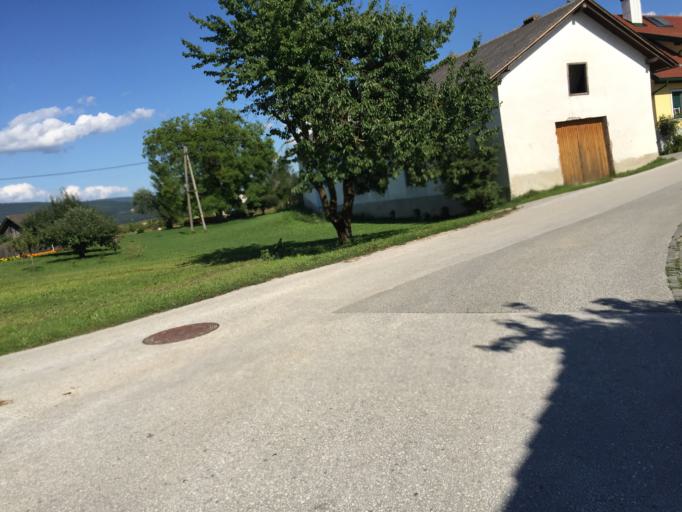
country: AT
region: Carinthia
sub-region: Politischer Bezirk Volkermarkt
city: Feistritz ob Bleiburg
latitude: 46.5716
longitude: 14.7648
